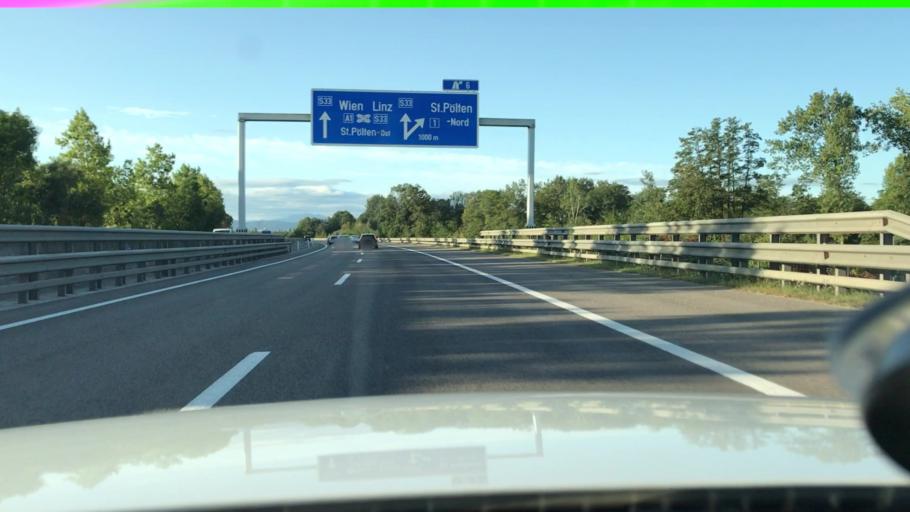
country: AT
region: Lower Austria
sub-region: Politischer Bezirk Sankt Polten
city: Herzogenburg
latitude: 48.2441
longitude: 15.6830
